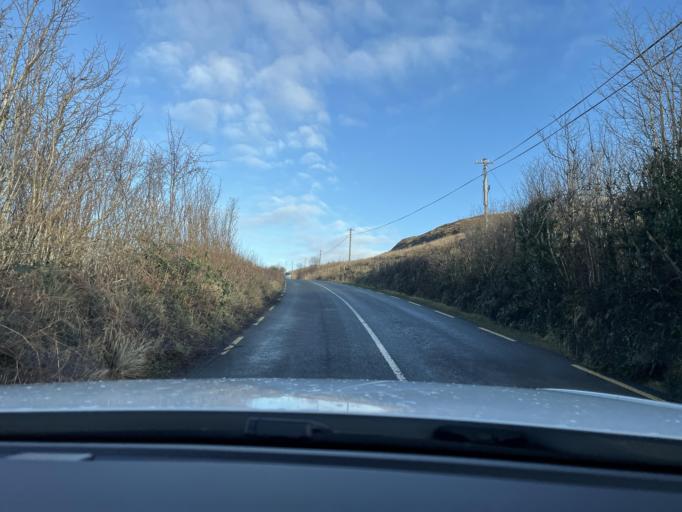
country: IE
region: Connaught
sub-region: County Leitrim
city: Manorhamilton
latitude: 54.2786
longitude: -8.2687
